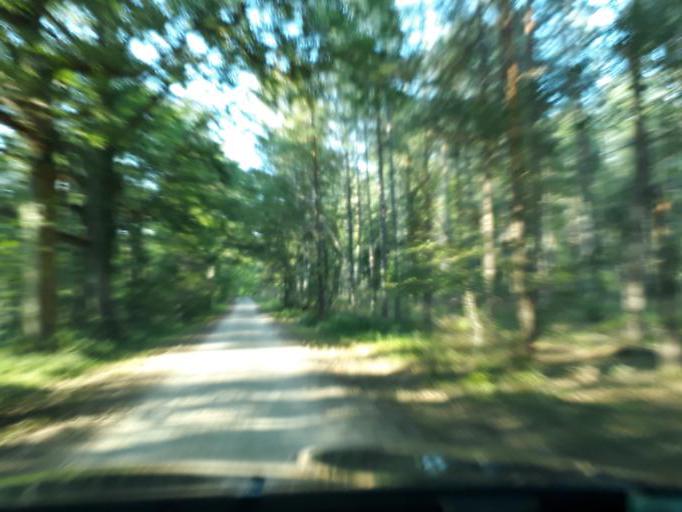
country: FR
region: Centre
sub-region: Departement du Loiret
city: Chaingy
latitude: 47.9078
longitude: 1.7416
